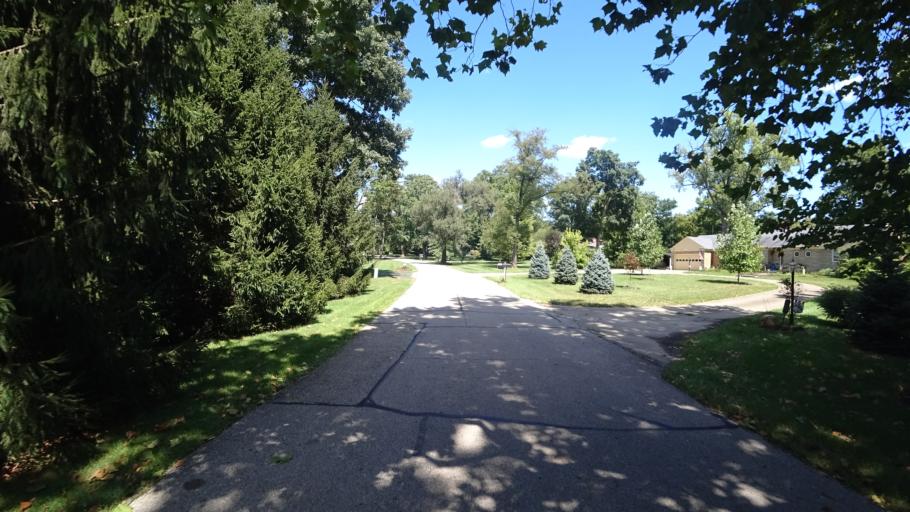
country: US
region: Ohio
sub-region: Butler County
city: New Miami
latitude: 39.4068
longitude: -84.5169
